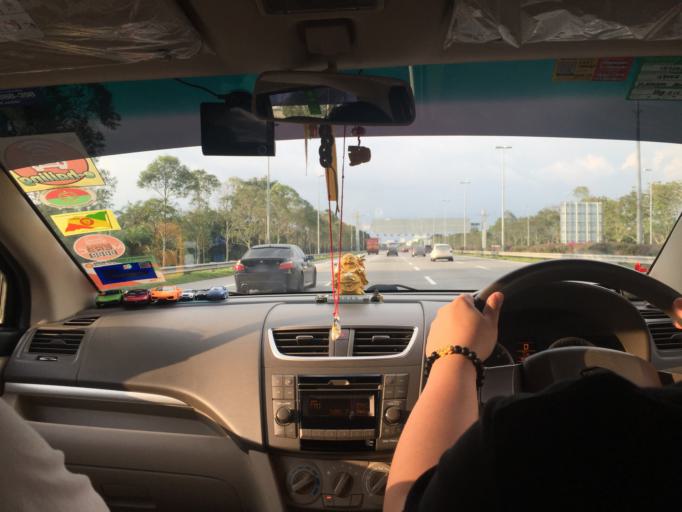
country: MY
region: Negeri Sembilan
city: Kampung Baharu Nilai
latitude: 2.7900
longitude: 101.6727
